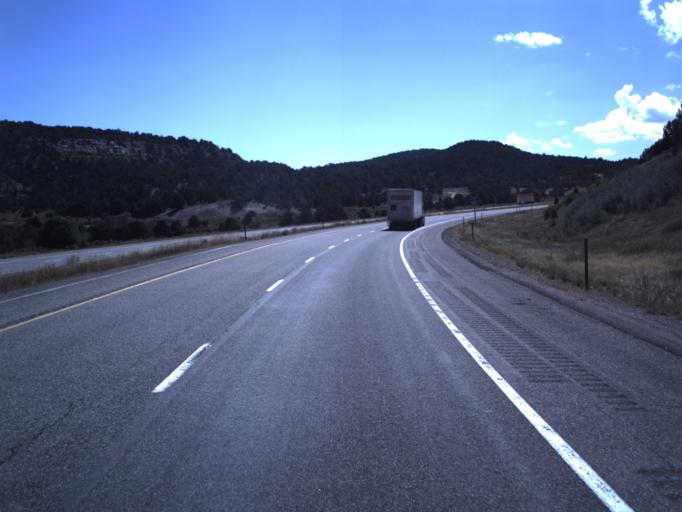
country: US
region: Utah
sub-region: Sevier County
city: Salina
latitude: 38.8753
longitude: -111.5552
